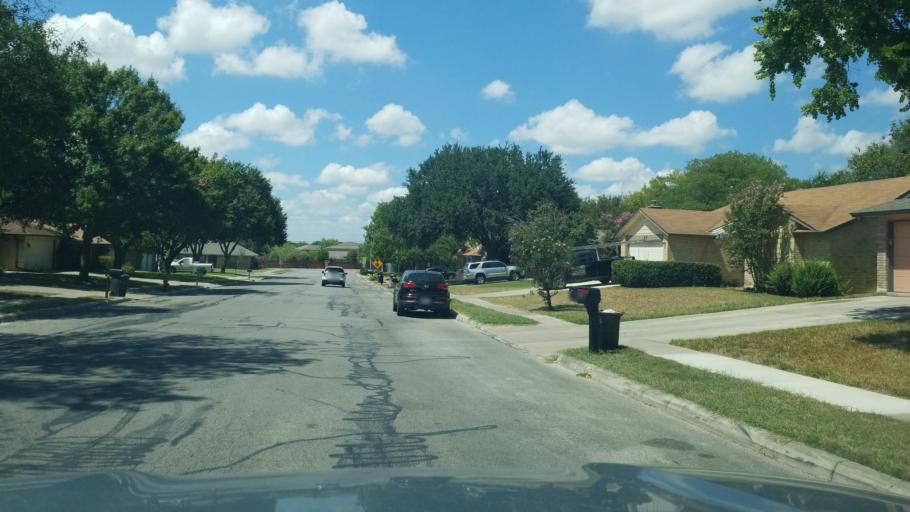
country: US
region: Texas
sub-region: Bexar County
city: Converse
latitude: 29.5392
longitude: -98.3150
